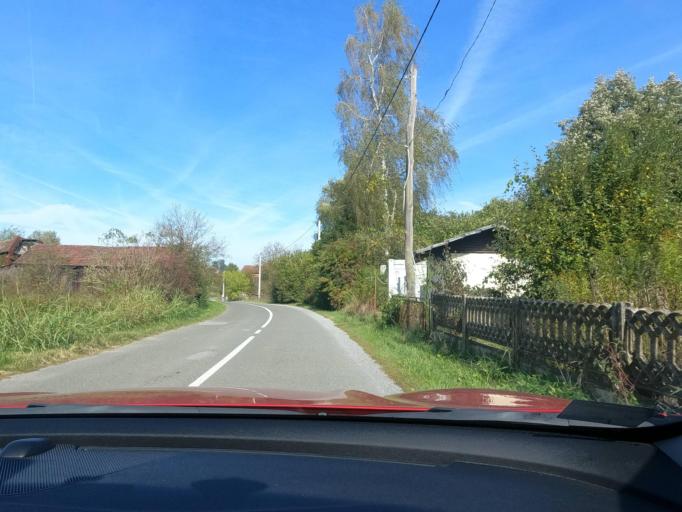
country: HR
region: Sisacko-Moslavacka
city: Petrinja
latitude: 45.3422
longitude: 16.2500
